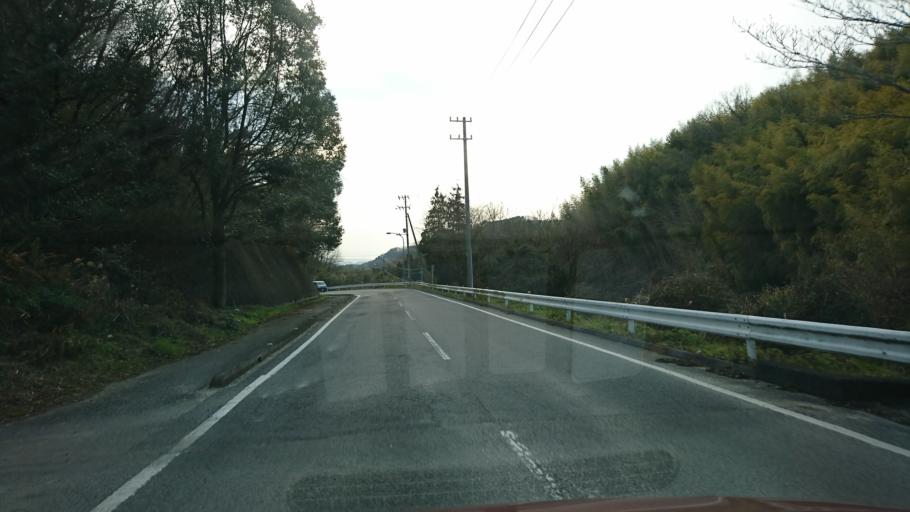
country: JP
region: Ehime
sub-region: Shikoku-chuo Shi
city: Matsuyama
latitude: 33.8993
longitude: 132.8069
